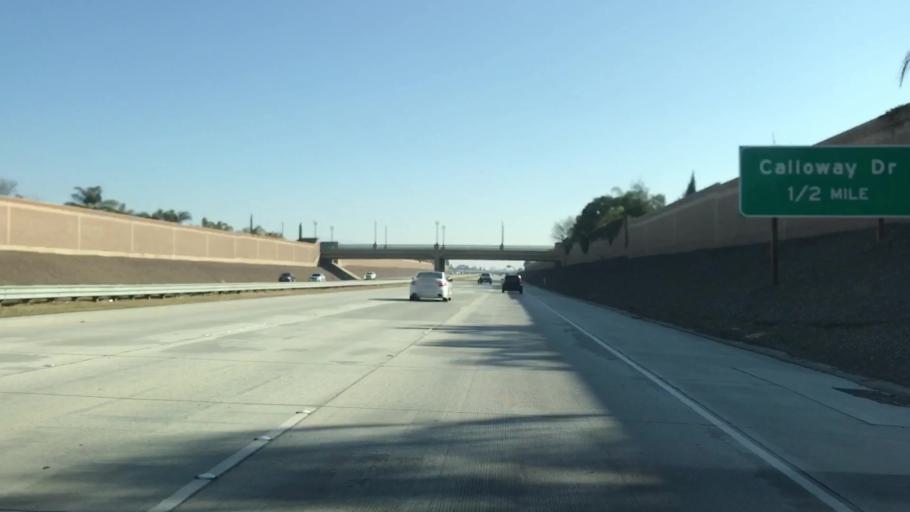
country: US
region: California
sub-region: Kern County
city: Rosedale
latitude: 35.3617
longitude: -119.1306
